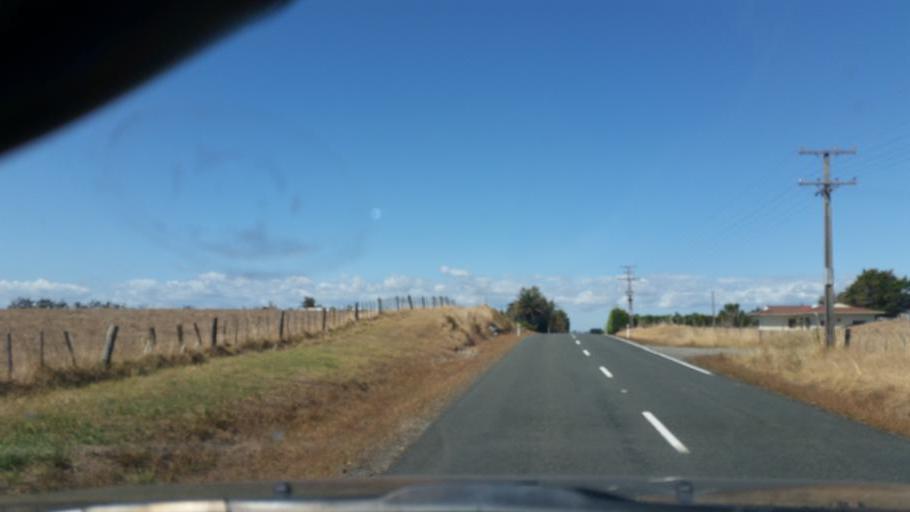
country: NZ
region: Northland
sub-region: Kaipara District
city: Dargaville
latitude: -35.9453
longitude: 173.8144
